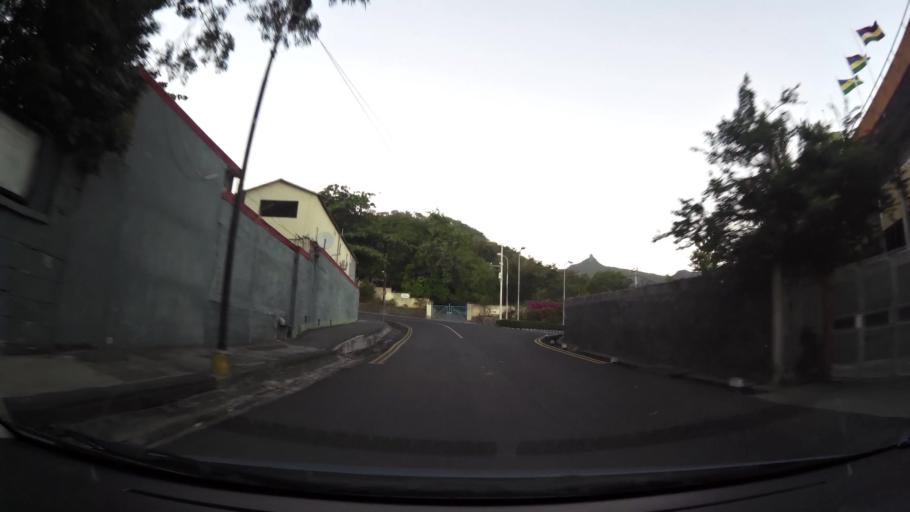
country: MU
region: Port Louis
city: Port Louis
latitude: -20.1693
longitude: 57.5130
